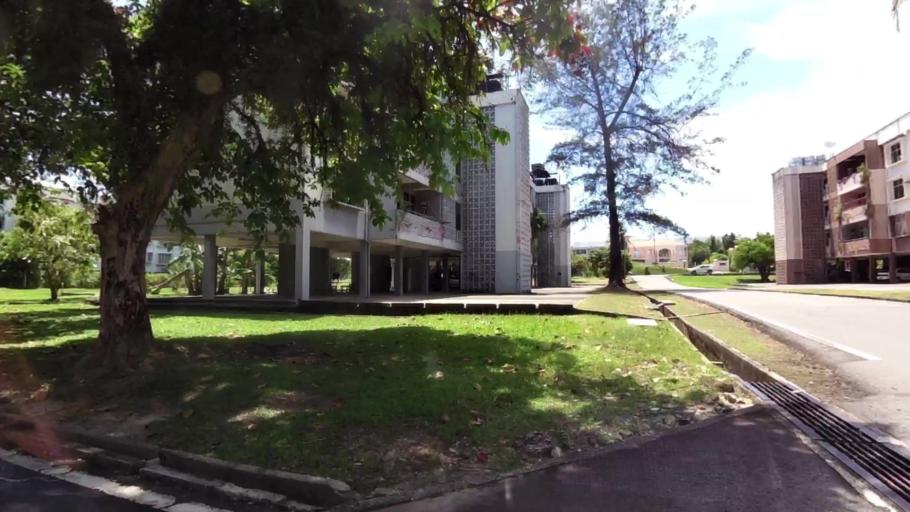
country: BN
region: Brunei and Muara
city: Bandar Seri Begawan
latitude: 4.9342
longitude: 114.9435
